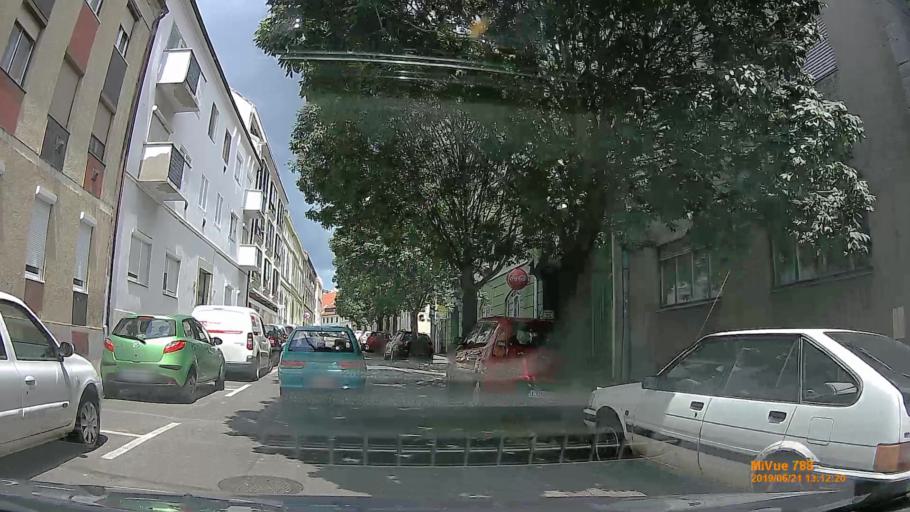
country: HU
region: Baranya
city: Pecs
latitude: 46.0747
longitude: 18.2348
